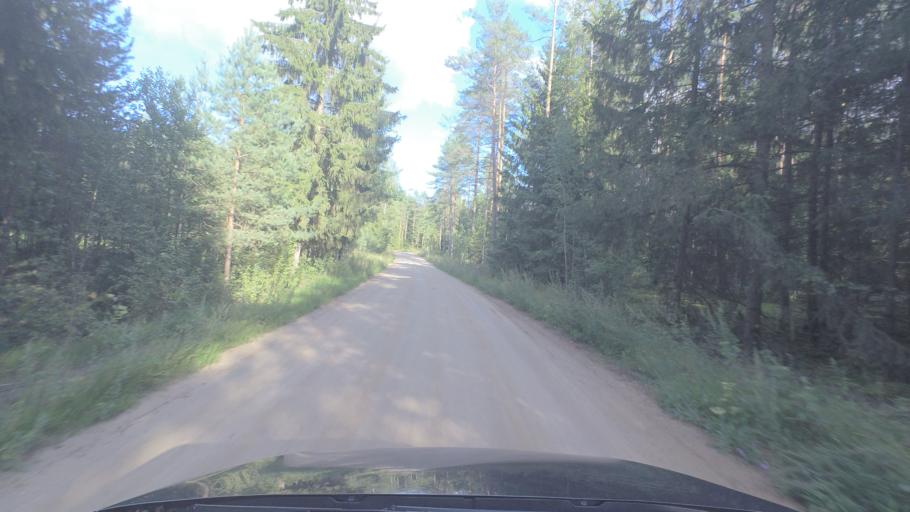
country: LT
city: Pabrade
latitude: 55.1478
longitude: 25.7555
